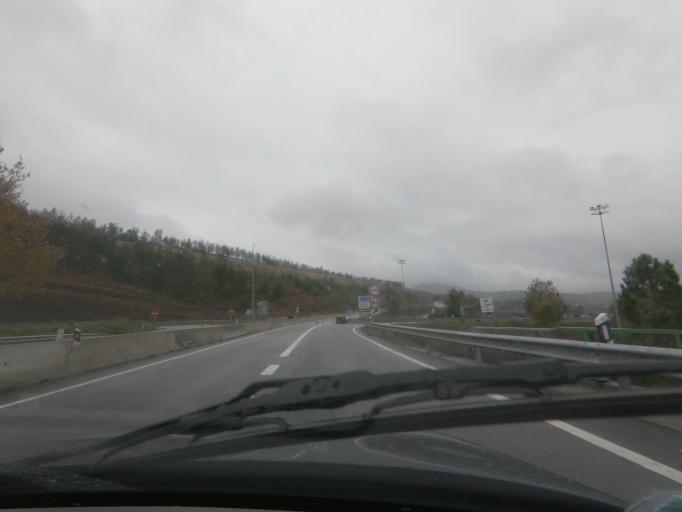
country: PT
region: Vila Real
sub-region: Santa Marta de Penaguiao
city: Santa Marta de Penaguiao
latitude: 41.2812
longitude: -7.8422
